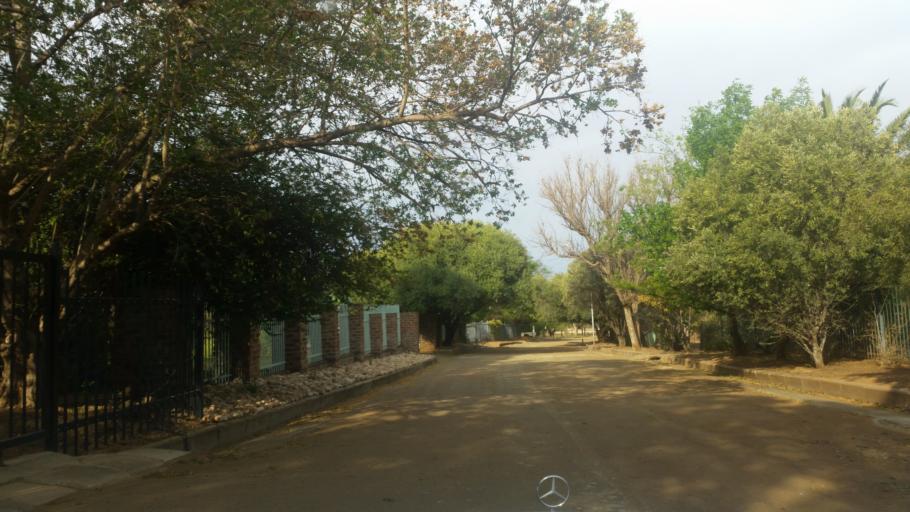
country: ZA
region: Orange Free State
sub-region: Xhariep District Municipality
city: Trompsburg
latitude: -30.4937
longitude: 25.9674
